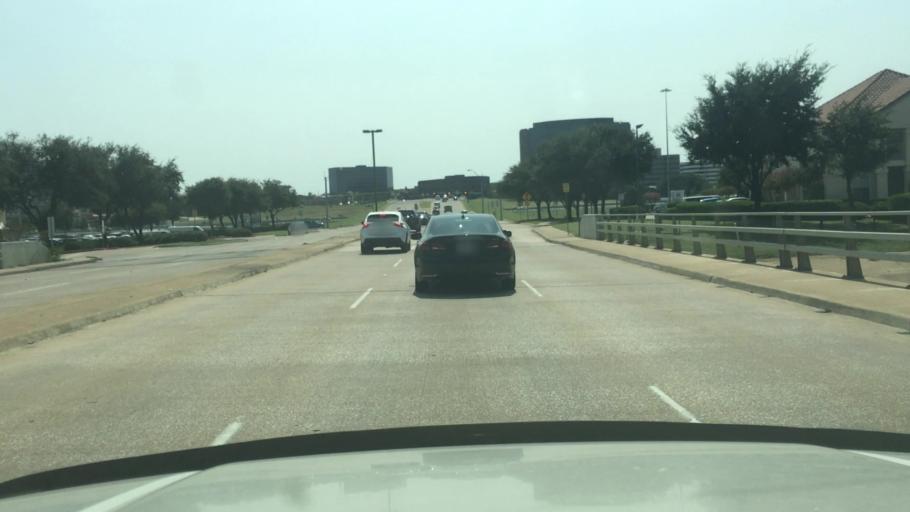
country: US
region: Texas
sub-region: Dallas County
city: Farmers Branch
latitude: 32.8934
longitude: -96.9603
